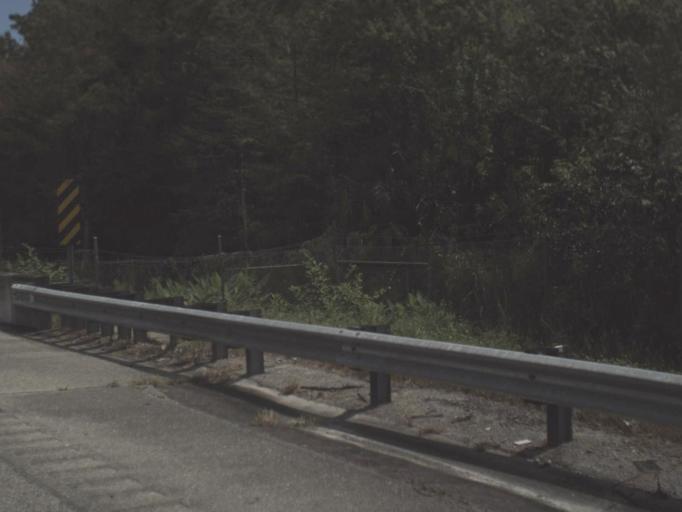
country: US
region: Florida
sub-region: Collier County
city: Immokalee
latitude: 26.1648
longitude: -81.2455
